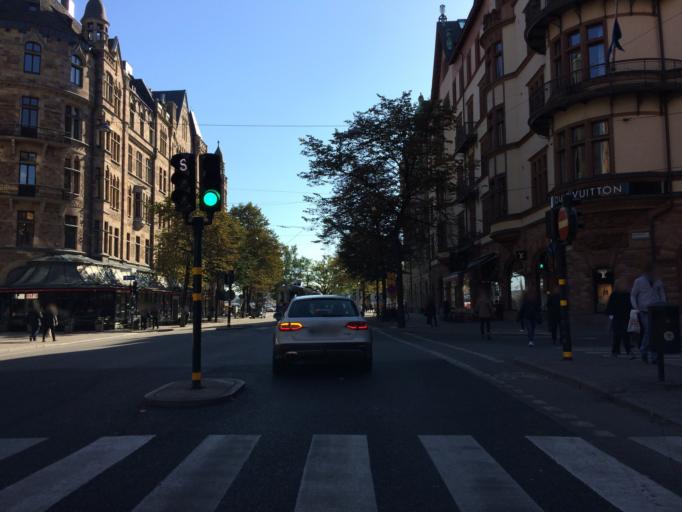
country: SE
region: Stockholm
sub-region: Stockholms Kommun
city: Stockholm
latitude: 59.3341
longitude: 18.0750
